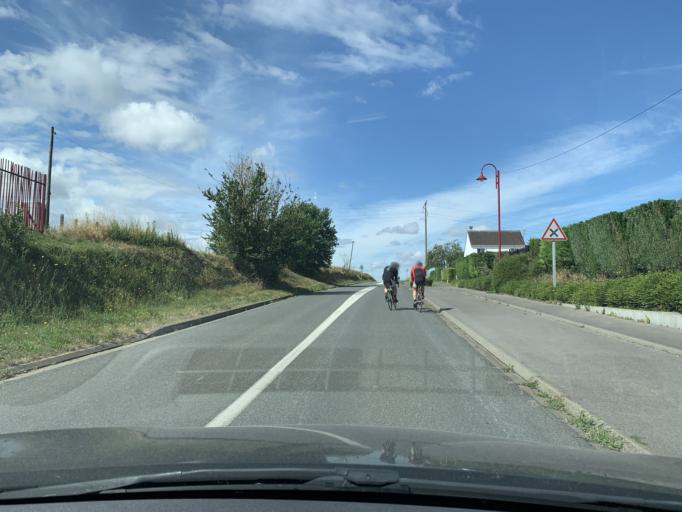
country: FR
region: Nord-Pas-de-Calais
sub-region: Departement du Nord
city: Proville
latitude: 50.1579
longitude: 3.2022
